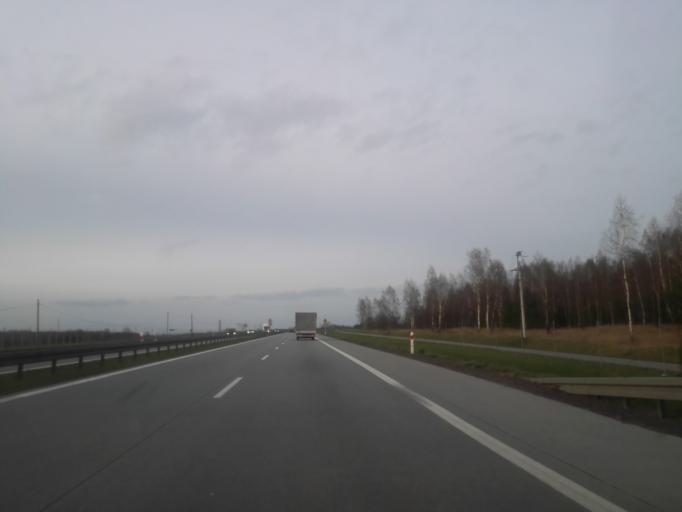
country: PL
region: Lodz Voivodeship
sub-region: Powiat skierniewicki
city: Kowiesy
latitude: 51.8699
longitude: 20.3857
